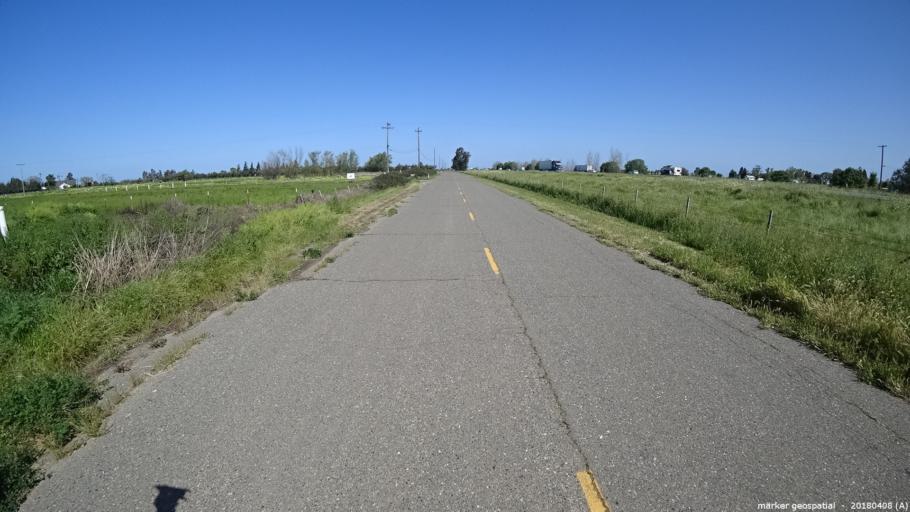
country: US
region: California
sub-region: Sacramento County
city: Walnut Grove
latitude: 38.3309
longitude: -121.4682
